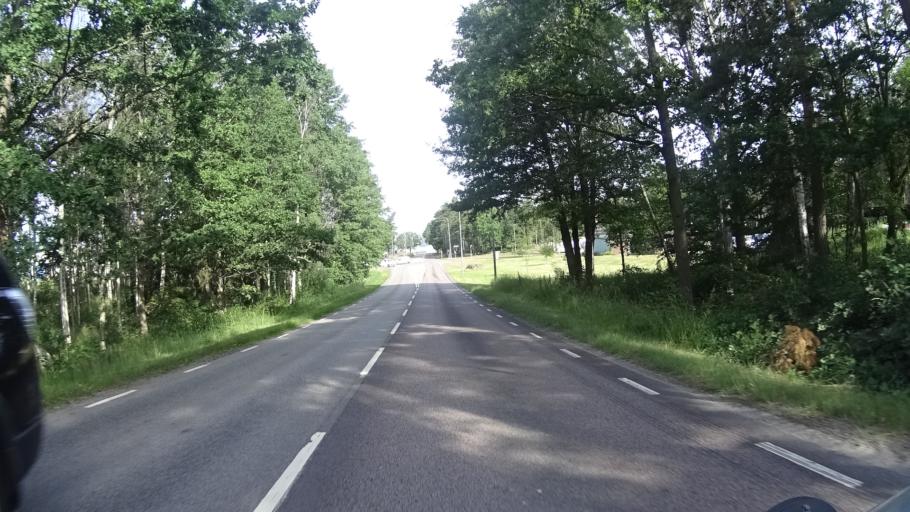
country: SE
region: Kalmar
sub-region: Oskarshamns Kommun
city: Oskarshamn
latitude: 57.2550
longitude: 16.4390
